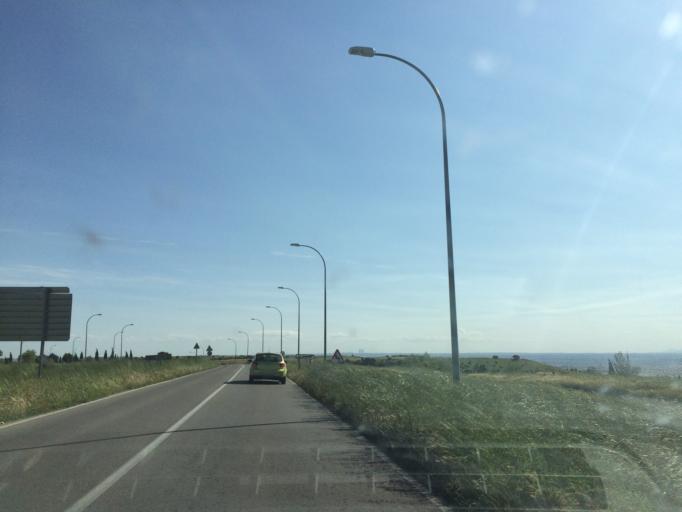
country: ES
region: Madrid
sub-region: Provincia de Madrid
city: Ribatejada
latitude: 40.6961
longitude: -3.4381
